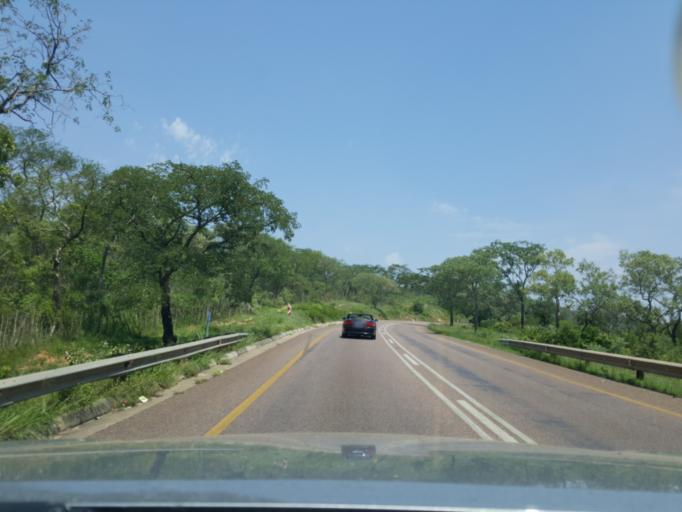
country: ZA
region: Mpumalanga
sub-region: Ehlanzeni District
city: Graksop
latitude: -25.0151
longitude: 31.1158
